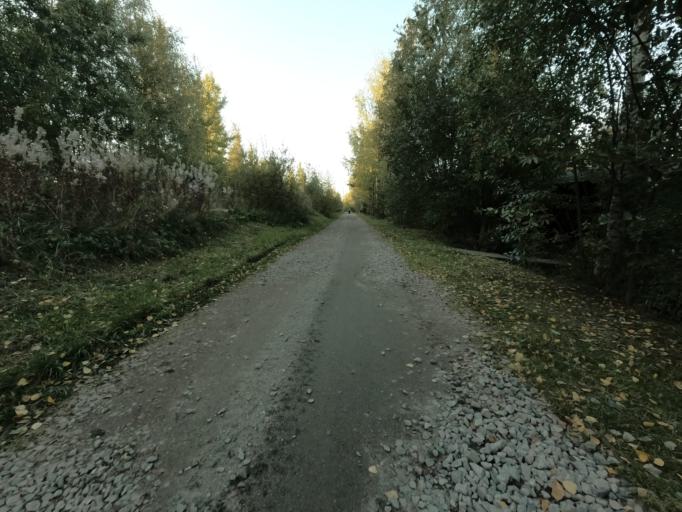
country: RU
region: Leningrad
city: Nikol'skoye
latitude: 59.7079
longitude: 30.7973
